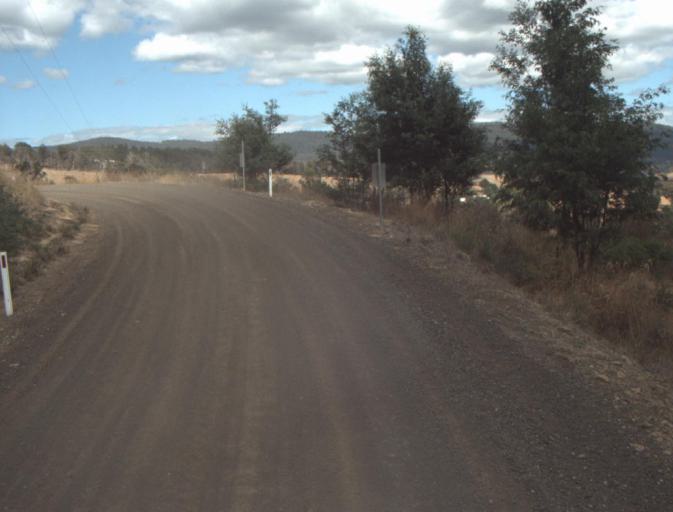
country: AU
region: Tasmania
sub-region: Launceston
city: Mayfield
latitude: -41.2177
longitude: 147.1677
